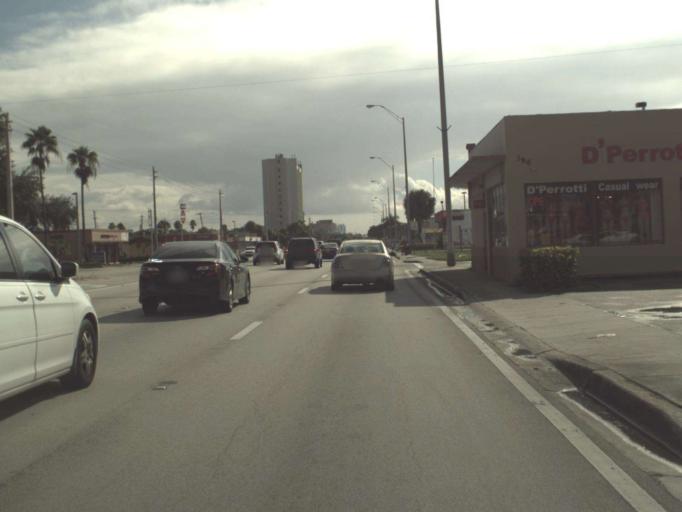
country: US
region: Florida
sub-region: Miami-Dade County
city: Golden Glades
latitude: 25.9283
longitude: -80.1928
